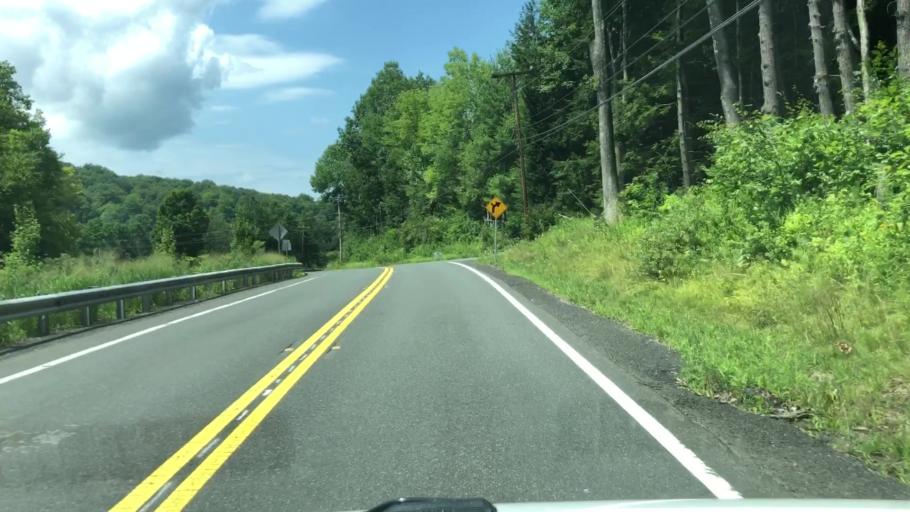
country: US
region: Massachusetts
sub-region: Franklin County
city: Conway
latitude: 42.5129
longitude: -72.7414
